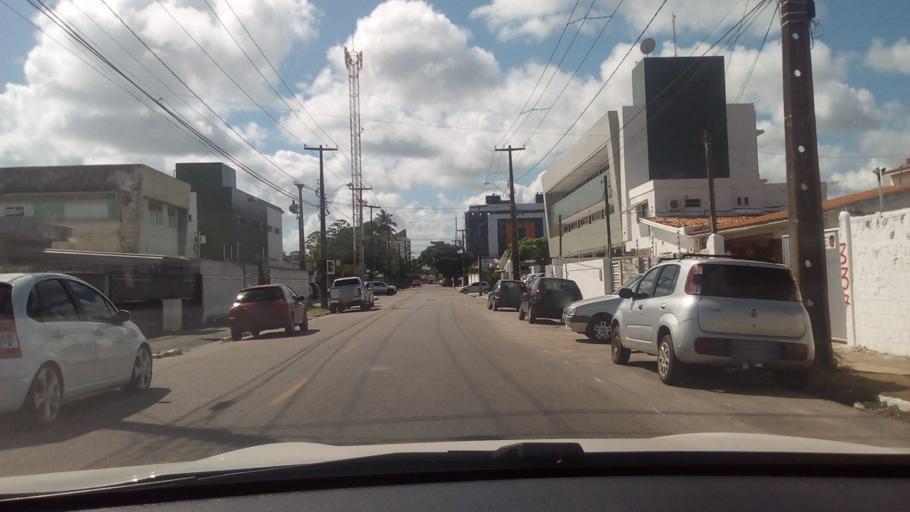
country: BR
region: Paraiba
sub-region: Joao Pessoa
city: Joao Pessoa
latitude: -7.1278
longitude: -34.8682
